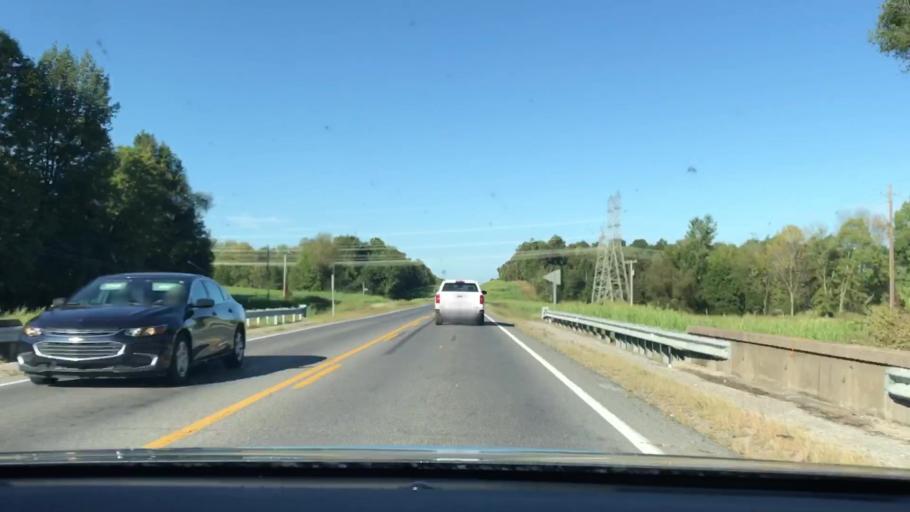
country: US
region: Kentucky
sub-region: Marshall County
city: Calvert City
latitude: 37.0050
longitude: -88.3920
